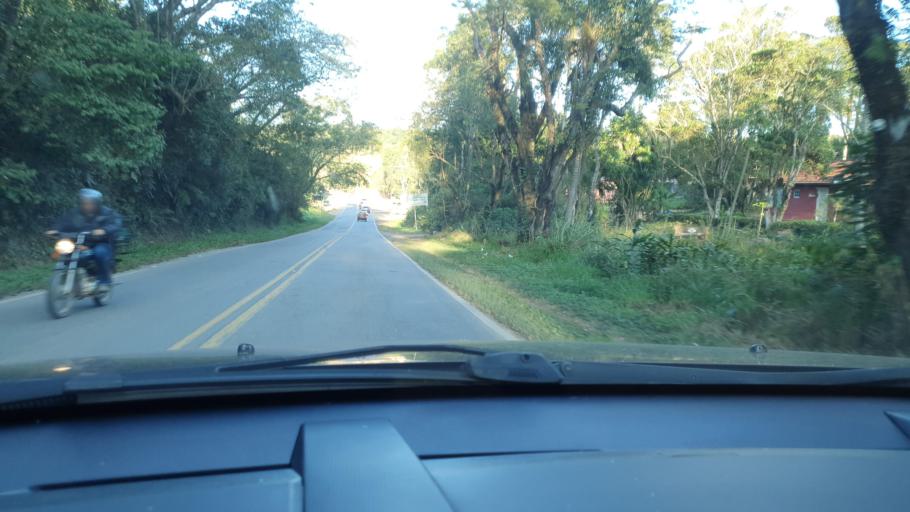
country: BR
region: Sao Paulo
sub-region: Piedade
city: Piedade
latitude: -23.6788
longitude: -47.3382
